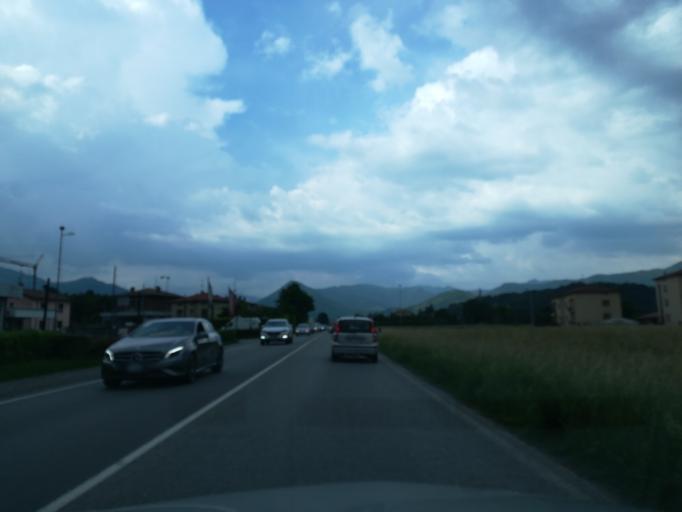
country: IT
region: Lombardy
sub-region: Provincia di Bergamo
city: Scano al Brembo
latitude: 45.7190
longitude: 9.6104
